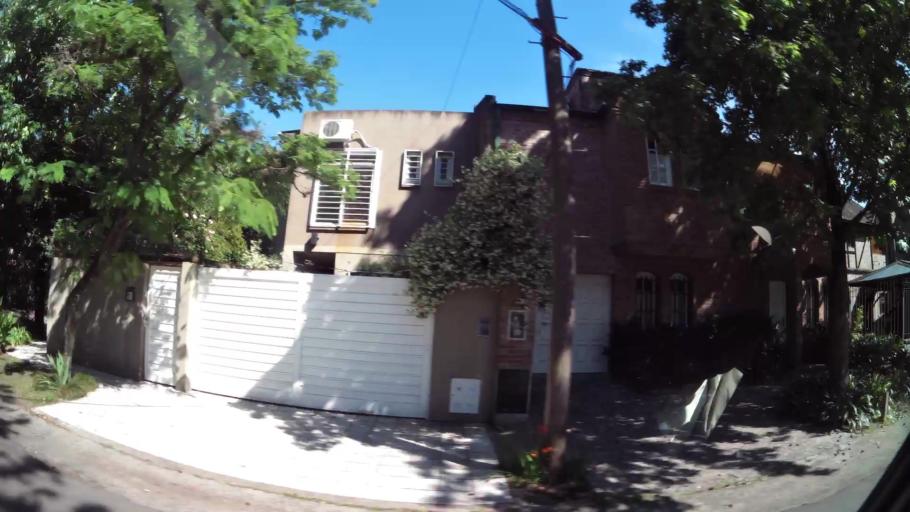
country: AR
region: Buenos Aires
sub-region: Partido de Tigre
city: Tigre
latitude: -34.4844
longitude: -58.5760
